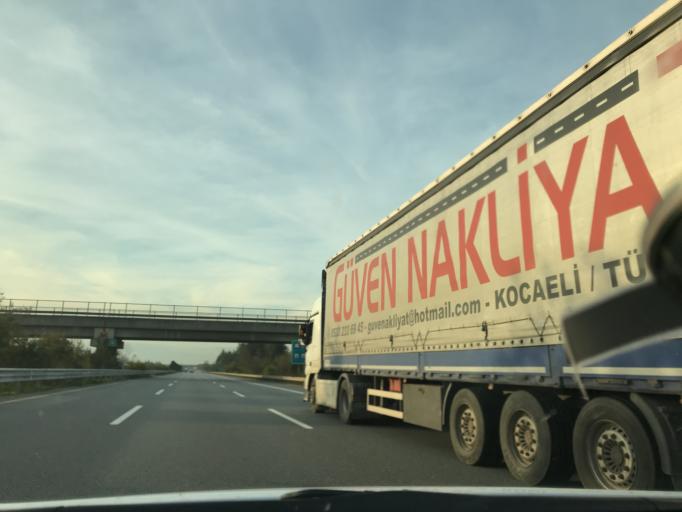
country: TR
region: Duzce
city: Cilimli
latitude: 40.8370
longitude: 31.0319
